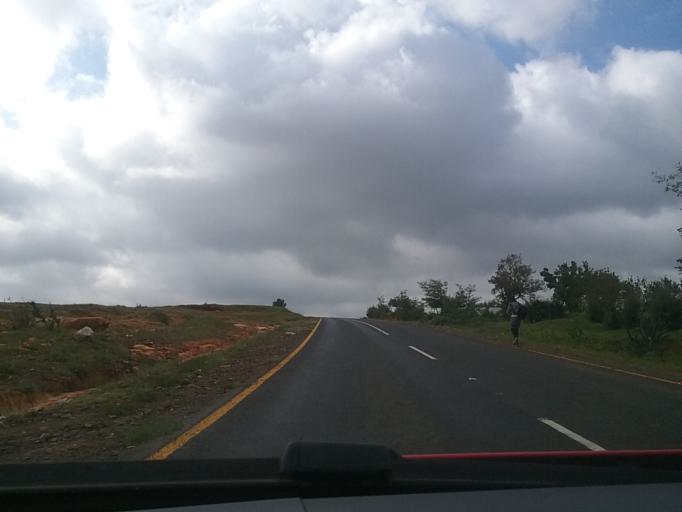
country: LS
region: Berea
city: Teyateyaneng
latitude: -29.1933
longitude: 27.8078
